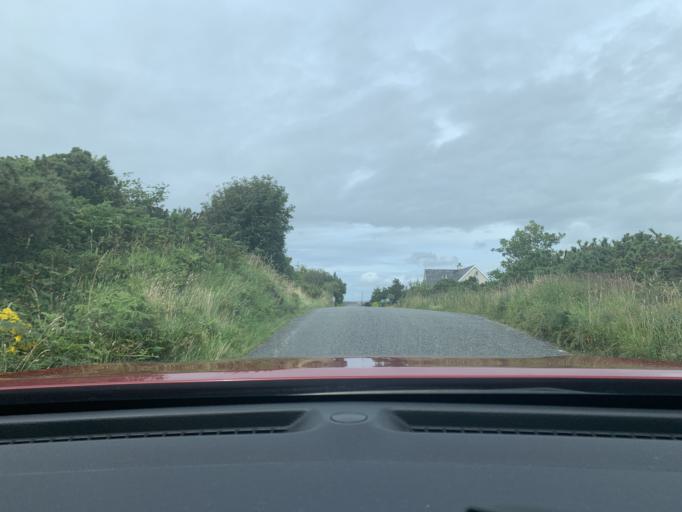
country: IE
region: Ulster
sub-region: County Donegal
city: Dungloe
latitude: 54.9415
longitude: -8.3591
